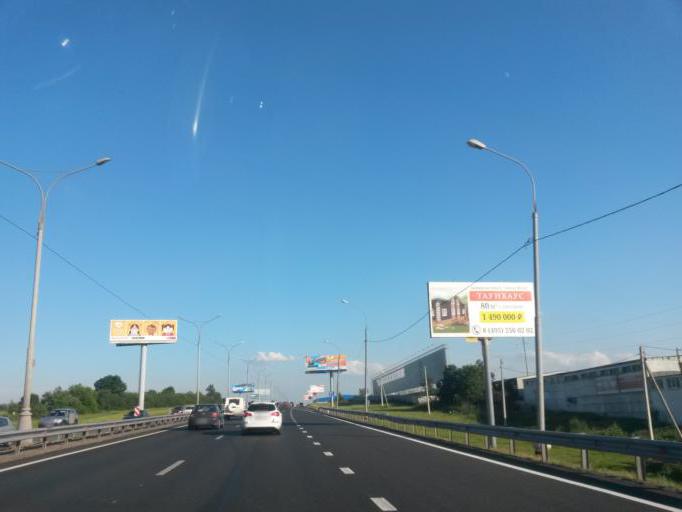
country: RU
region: Moskovskaya
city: Razvilka
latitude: 55.5748
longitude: 37.7604
